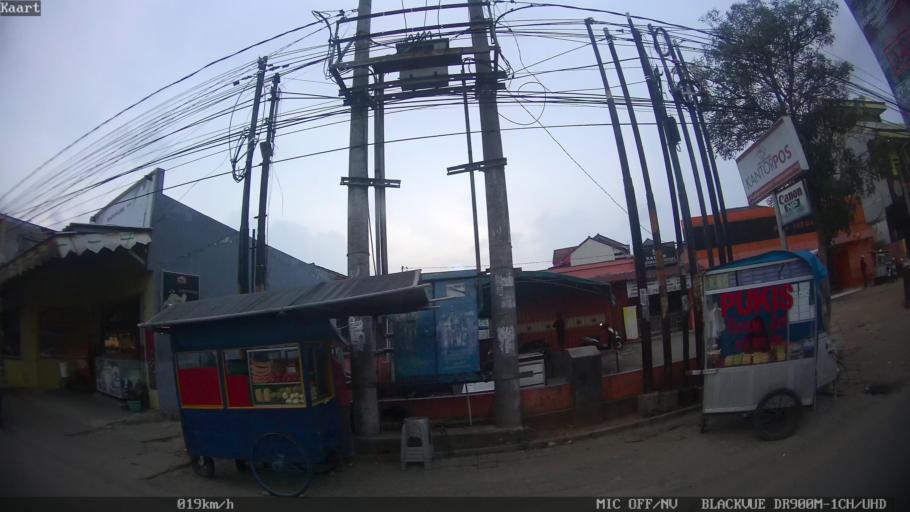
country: ID
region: Lampung
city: Bandarlampung
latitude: -5.4081
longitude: 105.2717
